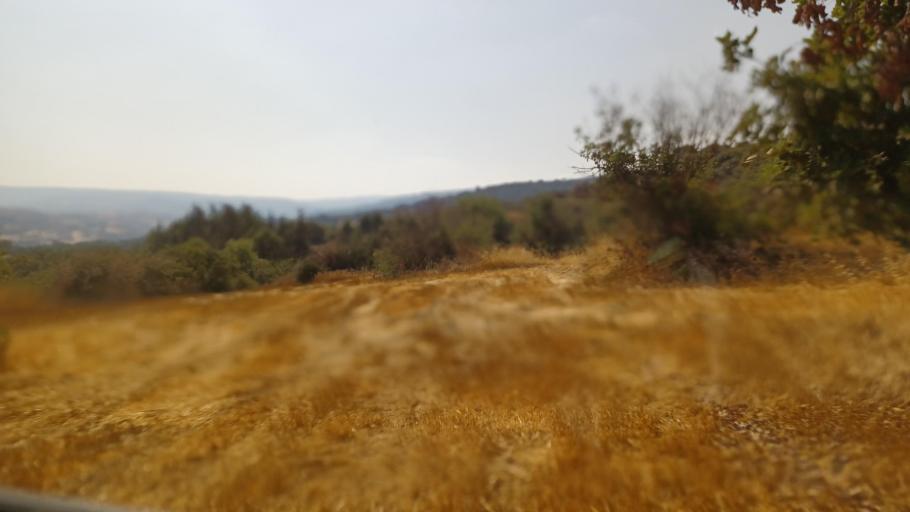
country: CY
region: Pafos
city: Polis
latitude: 34.9850
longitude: 32.4338
